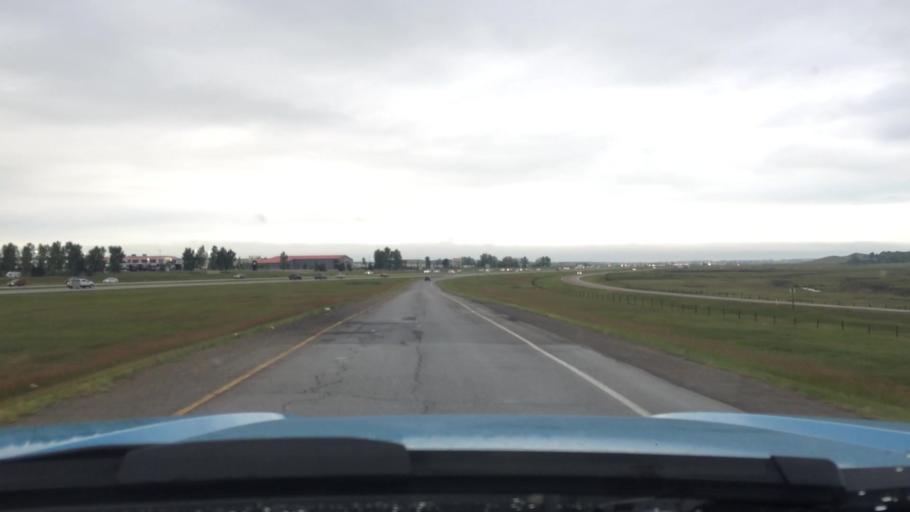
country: CA
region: Alberta
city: Airdrie
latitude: 51.2131
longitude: -113.9994
